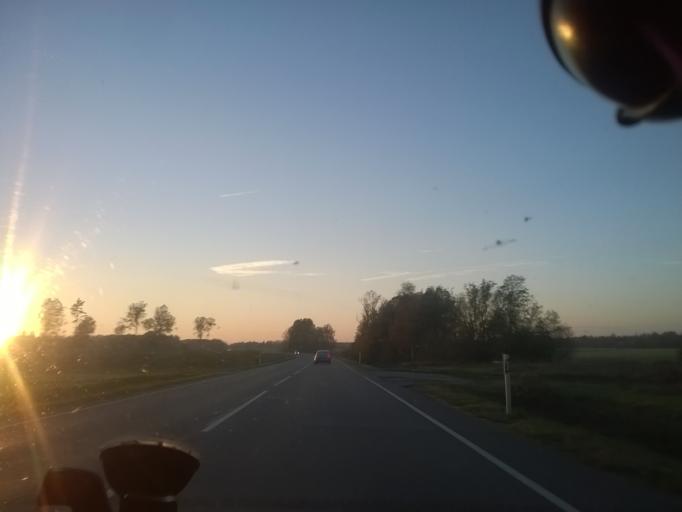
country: EE
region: Laeaene
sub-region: Ridala Parish
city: Uuemoisa
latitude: 58.9728
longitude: 23.8597
